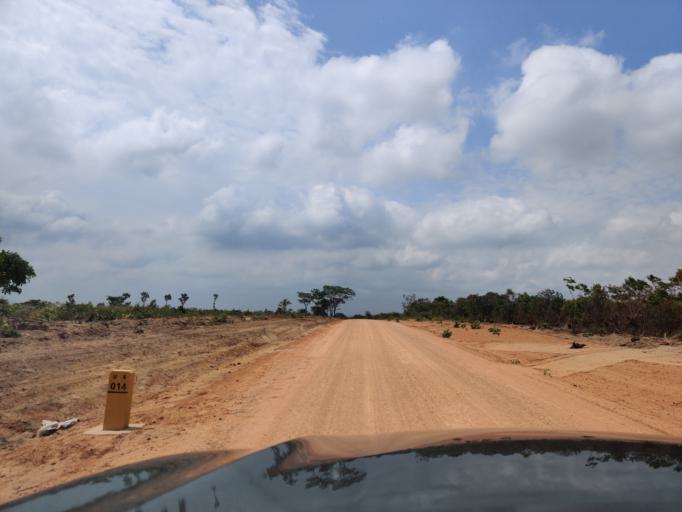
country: ZM
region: Central
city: Mkushi
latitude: -13.6659
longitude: 29.7509
